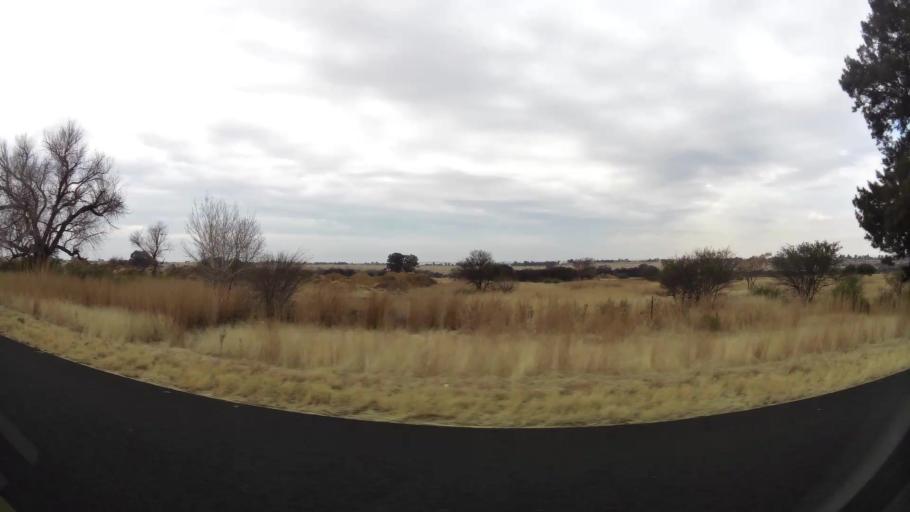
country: ZA
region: Orange Free State
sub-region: Fezile Dabi District Municipality
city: Kroonstad
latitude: -27.6398
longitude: 27.2477
